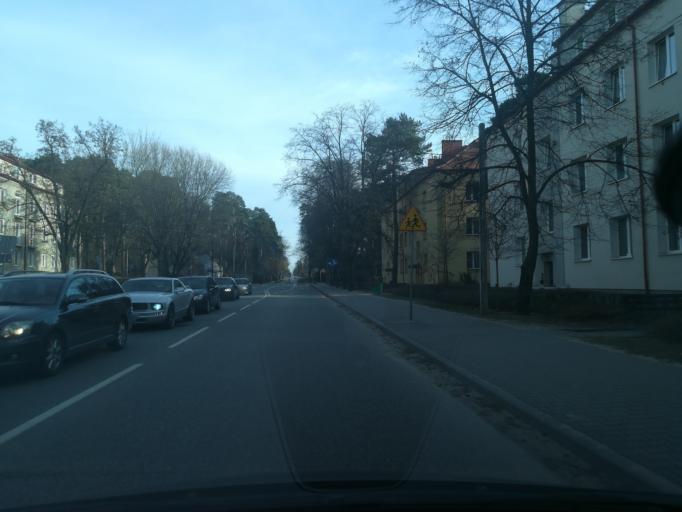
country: PL
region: Masovian Voivodeship
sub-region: Powiat piaseczynski
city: Konstancin-Jeziorna
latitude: 52.0875
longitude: 21.1246
